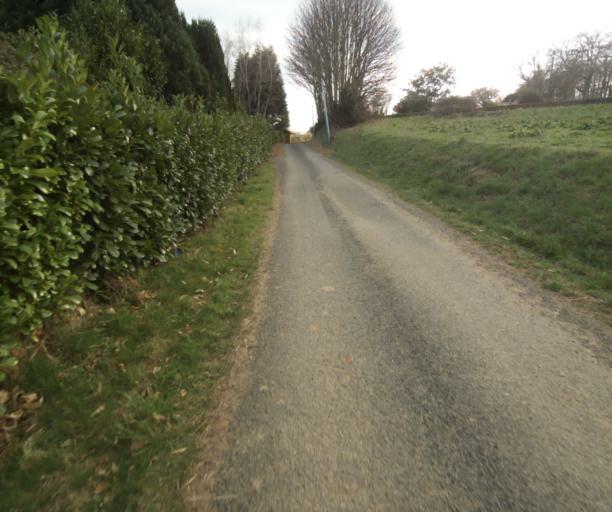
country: FR
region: Limousin
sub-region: Departement de la Correze
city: Saint-Clement
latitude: 45.3652
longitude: 1.6446
